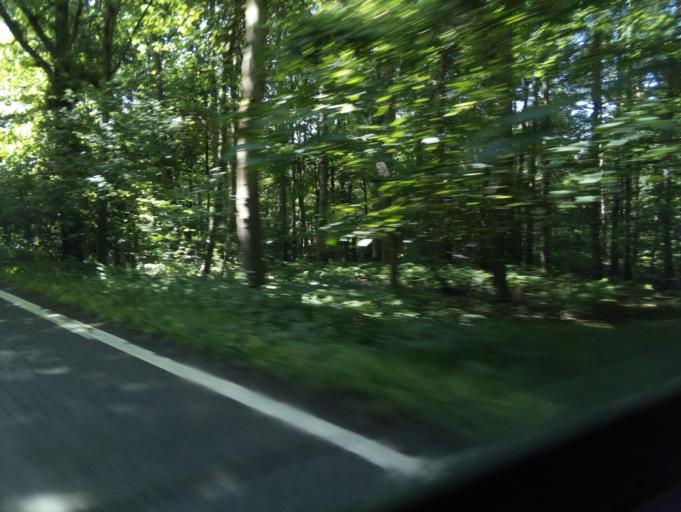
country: GB
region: England
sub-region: North Lincolnshire
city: Manton
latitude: 53.5414
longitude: -0.5769
